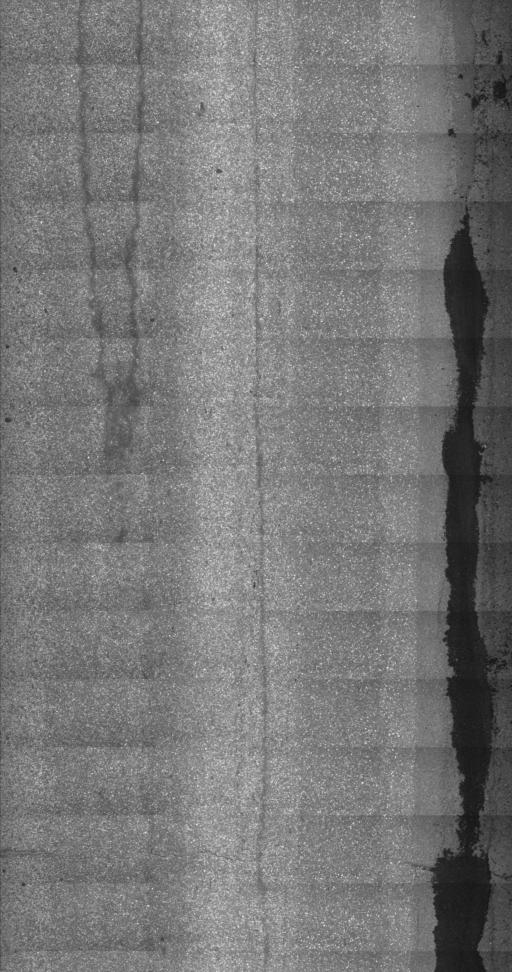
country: US
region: Vermont
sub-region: Washington County
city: Waterbury
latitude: 44.3313
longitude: -72.7499
